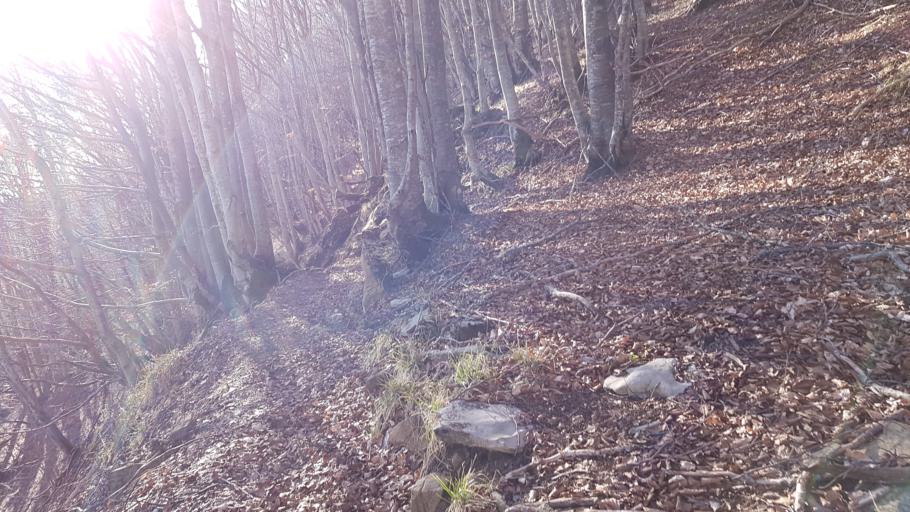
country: IT
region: Liguria
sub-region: Provincia di Genova
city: Propata
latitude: 44.5513
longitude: 9.1552
